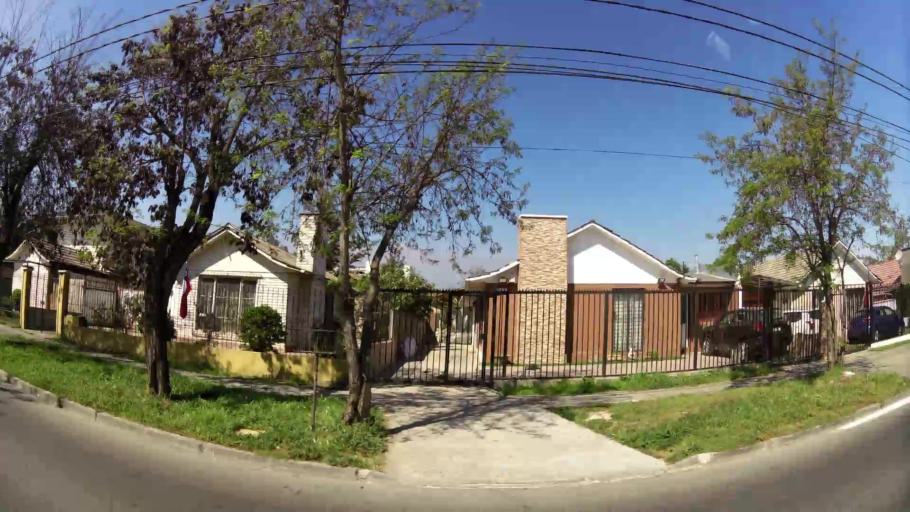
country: CL
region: Santiago Metropolitan
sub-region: Provincia de Santiago
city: Villa Presidente Frei, Nunoa, Santiago, Chile
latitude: -33.4889
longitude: -70.5869
